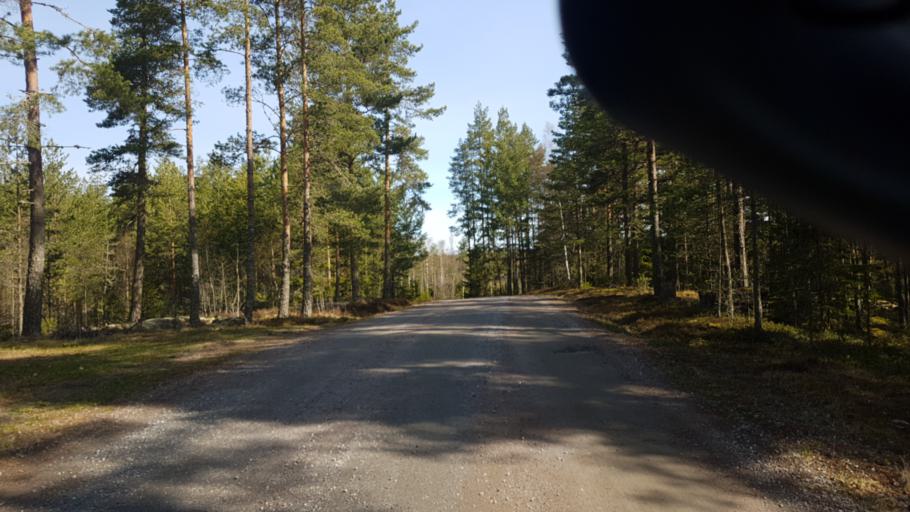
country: SE
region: Vaermland
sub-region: Arvika Kommun
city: Arvika
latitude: 59.5585
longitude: 12.7438
